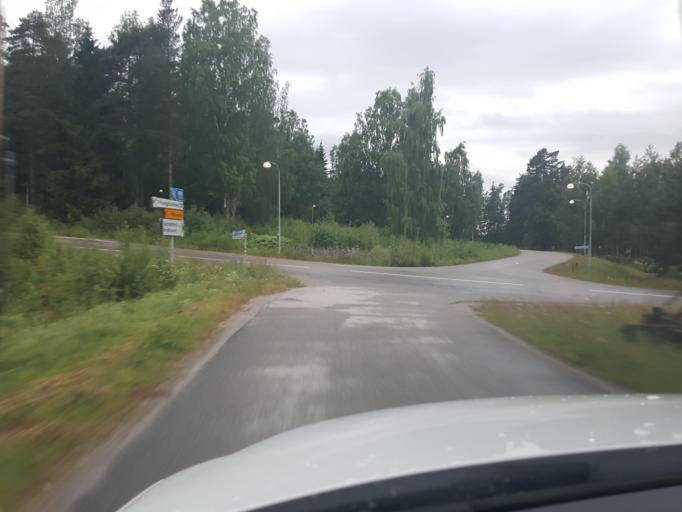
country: SE
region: Gaevleborg
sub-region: Bollnas Kommun
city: Kilafors
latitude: 61.2642
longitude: 16.6376
